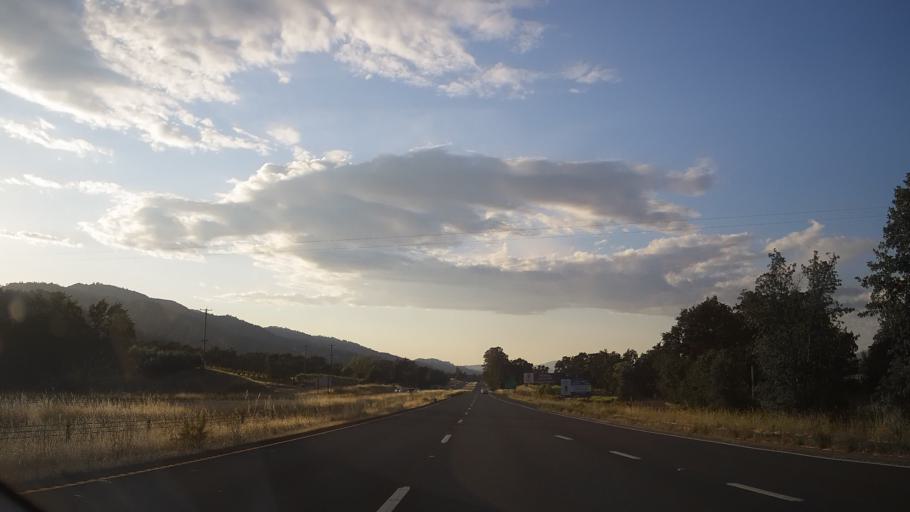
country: US
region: California
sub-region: Mendocino County
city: Talmage
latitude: 39.0854
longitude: -123.1829
